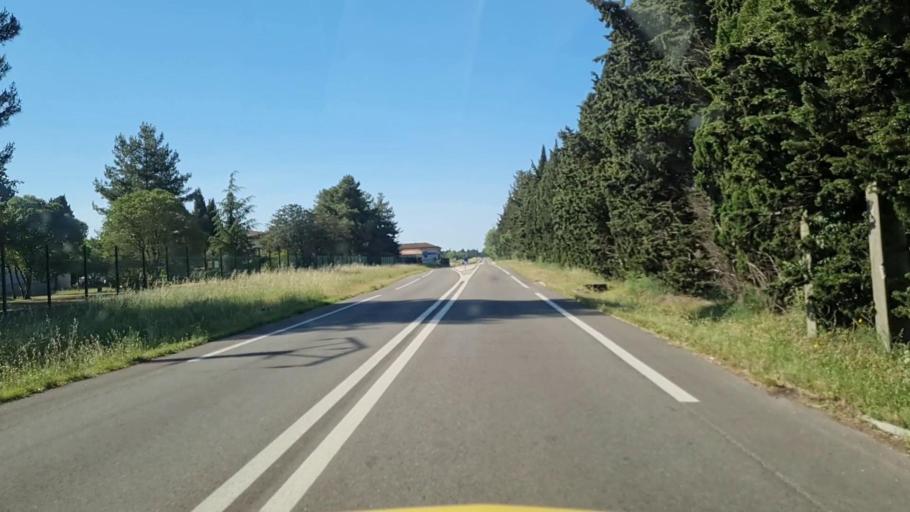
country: FR
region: Languedoc-Roussillon
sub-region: Departement du Gard
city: Garons
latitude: 43.7623
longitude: 4.4058
